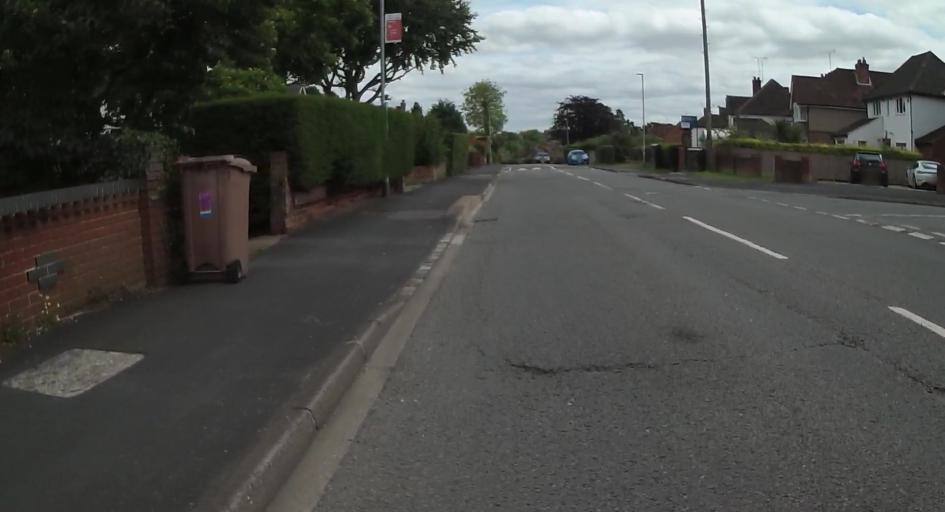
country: GB
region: England
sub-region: Wokingham
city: Earley
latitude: 51.4350
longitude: -0.9324
